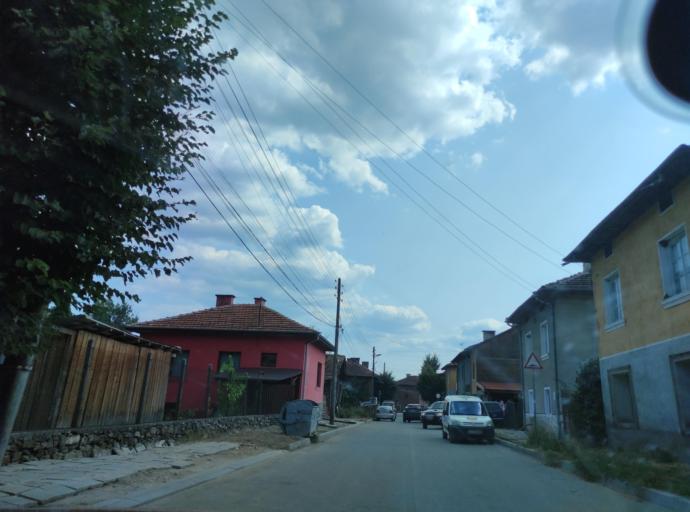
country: BG
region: Blagoevgrad
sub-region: Obshtina Belitsa
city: Belitsa
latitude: 41.9535
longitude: 23.5564
